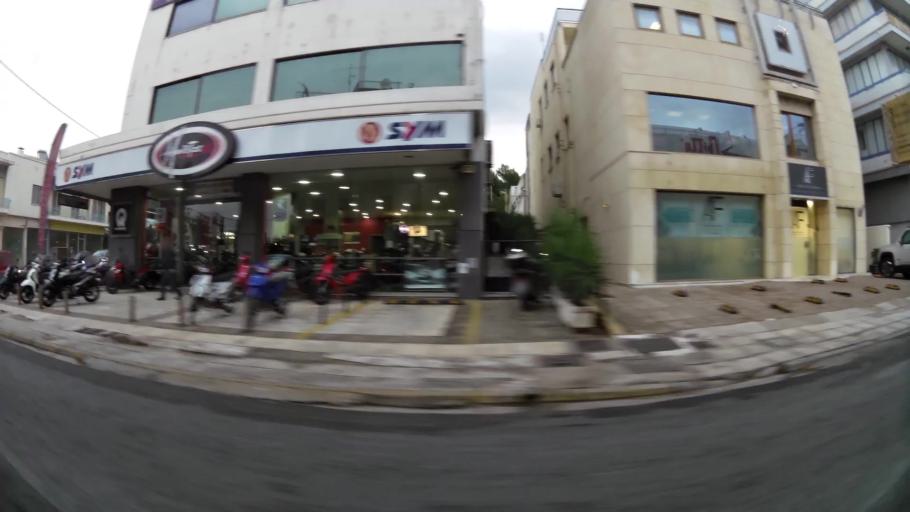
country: GR
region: Attica
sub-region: Nomarchia Athinas
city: Dhafni
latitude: 37.9462
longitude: 23.7391
